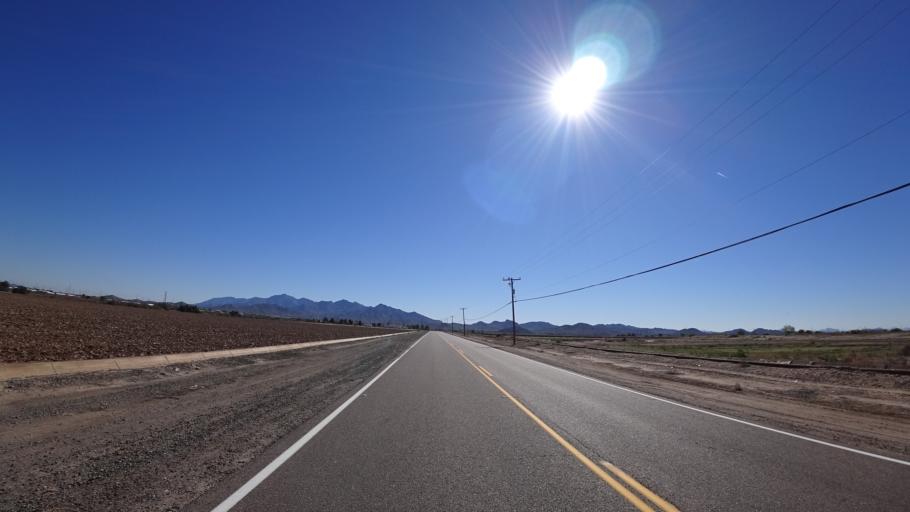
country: US
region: Arizona
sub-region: Maricopa County
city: Goodyear
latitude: 33.4181
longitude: -112.3577
